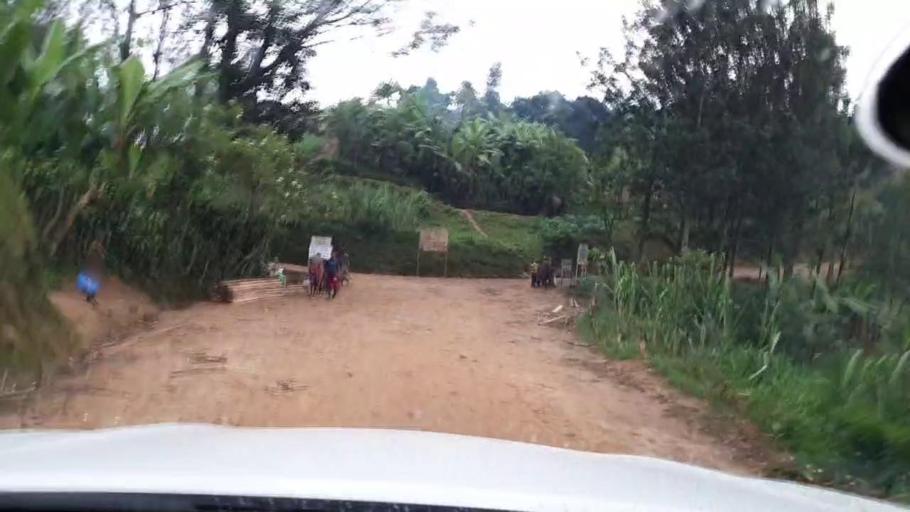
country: RW
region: Western Province
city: Cyangugu
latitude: -2.4066
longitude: 29.2086
